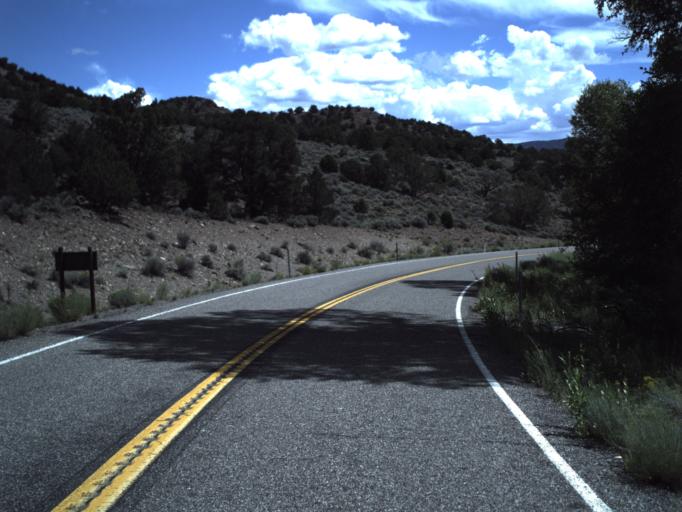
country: US
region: Utah
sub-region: Piute County
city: Junction
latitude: 38.2590
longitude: -112.2756
